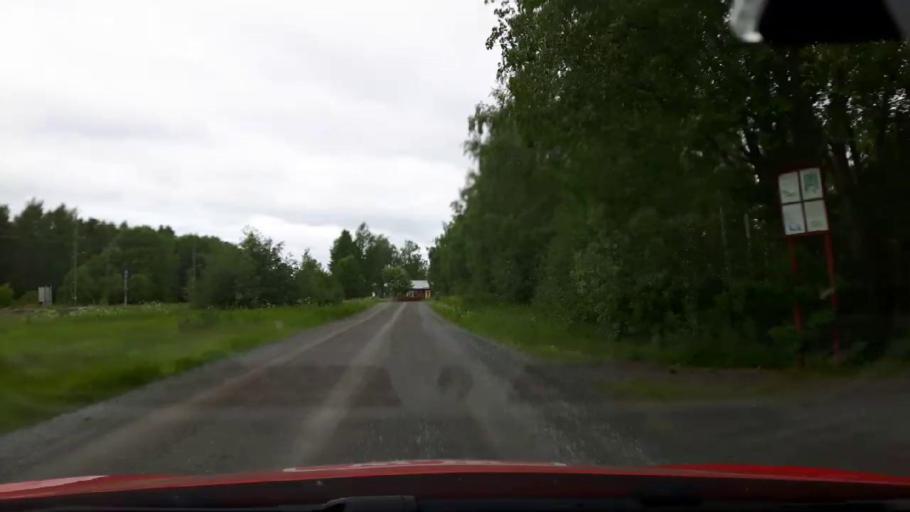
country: SE
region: Jaemtland
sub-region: Krokoms Kommun
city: Krokom
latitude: 63.2464
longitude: 14.5303
